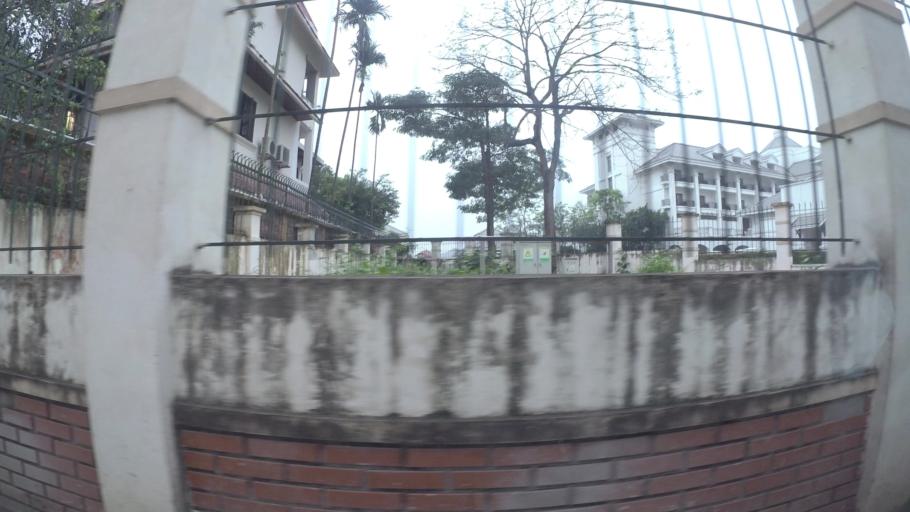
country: VN
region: Ha Noi
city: Tay Ho
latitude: 21.0580
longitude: 105.8324
